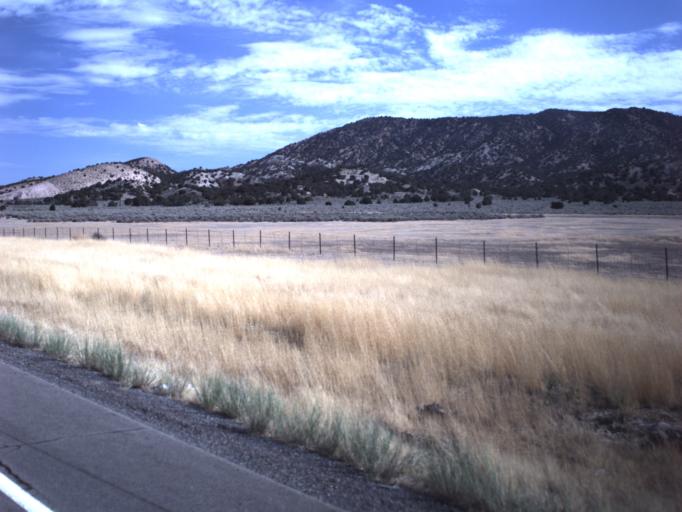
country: US
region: Utah
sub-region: Sanpete County
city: Gunnison
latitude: 39.3942
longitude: -111.9279
